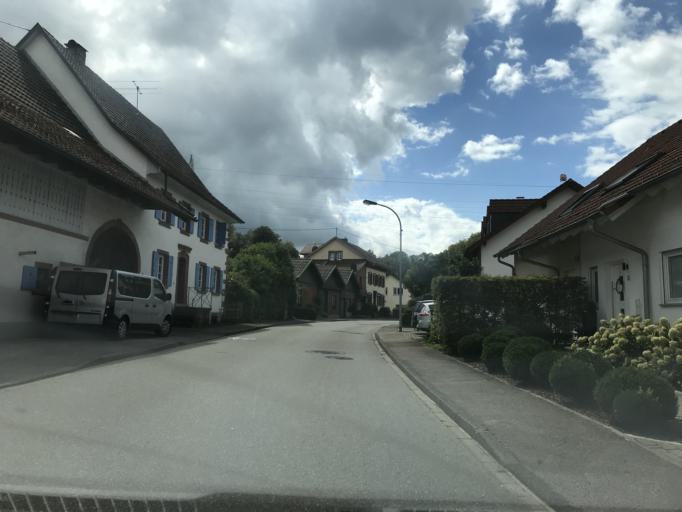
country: DE
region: Baden-Wuerttemberg
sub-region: Freiburg Region
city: Maulburg
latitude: 47.6405
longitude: 7.7781
